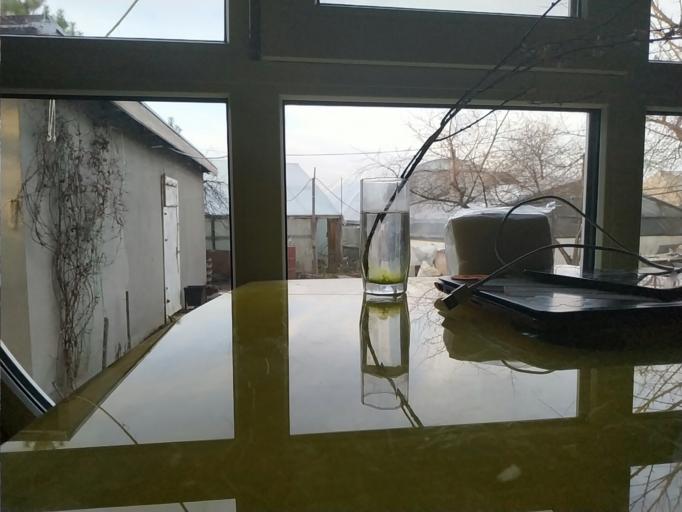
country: RU
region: Republic of Karelia
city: Suoyarvi
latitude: 62.2761
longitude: 32.0835
